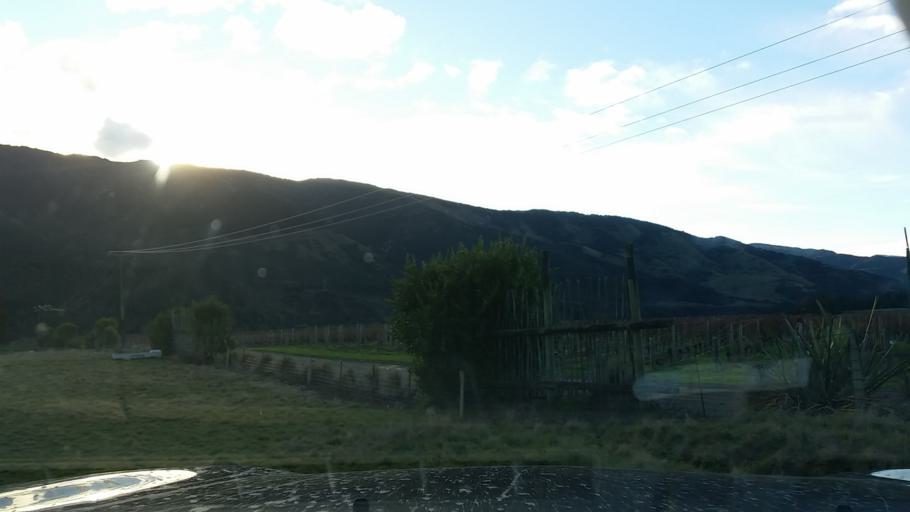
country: NZ
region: Marlborough
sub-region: Marlborough District
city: Blenheim
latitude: -41.7401
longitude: 173.8730
